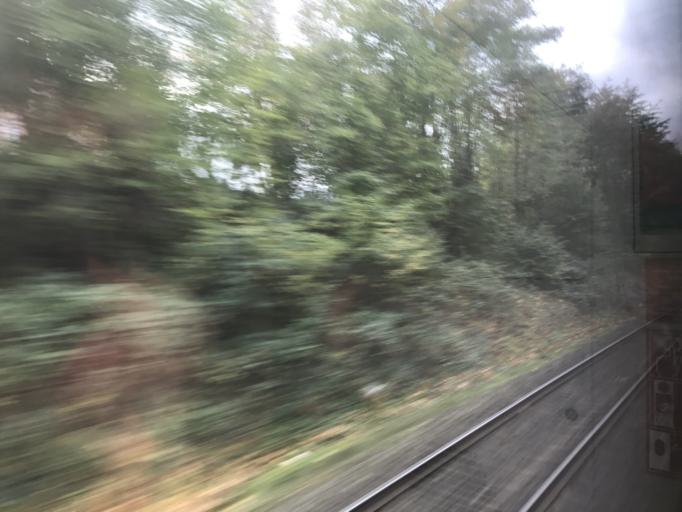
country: DE
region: North Rhine-Westphalia
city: Wetter (Ruhr)
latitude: 51.3831
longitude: 7.3935
